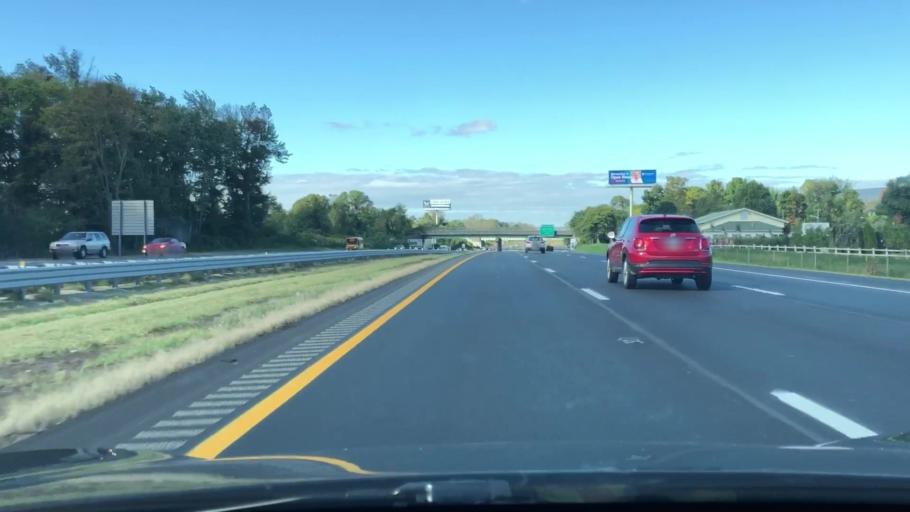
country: US
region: New Jersey
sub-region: Mercer County
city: Ewing
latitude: 40.2895
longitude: -74.7948
